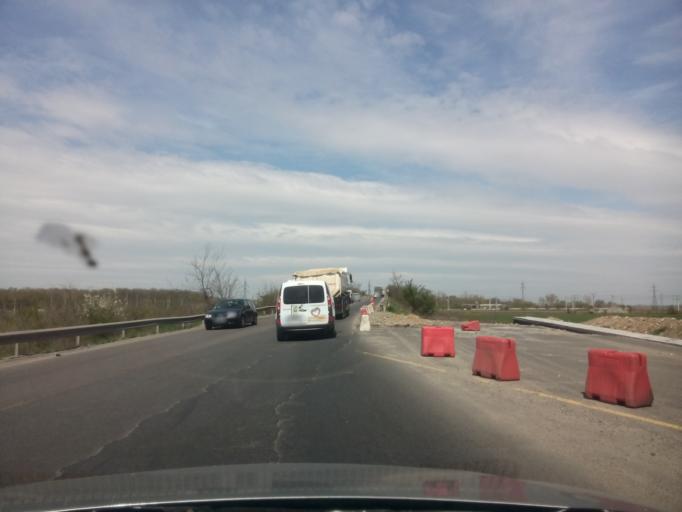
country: RO
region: Ilfov
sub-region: Comuna Pantelimon
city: Pantelimon
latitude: 44.4706
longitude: 26.2319
